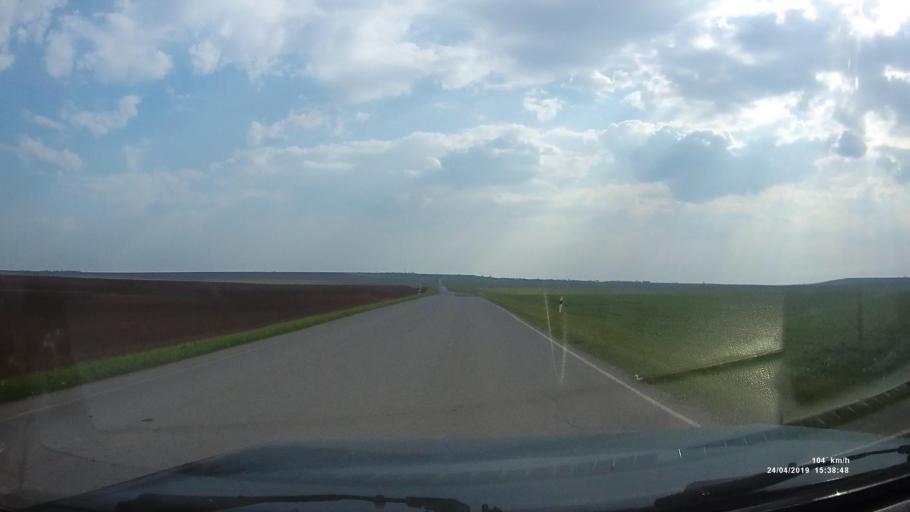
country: RU
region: Kalmykiya
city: Yashalta
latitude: 46.5936
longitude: 42.8229
